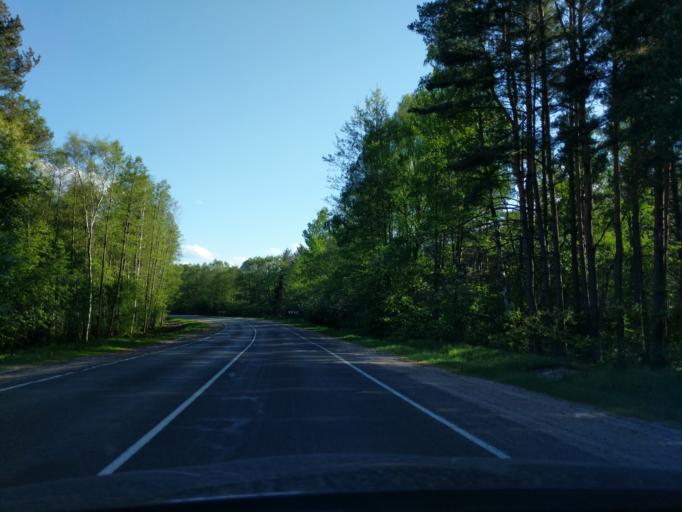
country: BY
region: Minsk
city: Myadzyel
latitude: 54.8448
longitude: 26.9259
